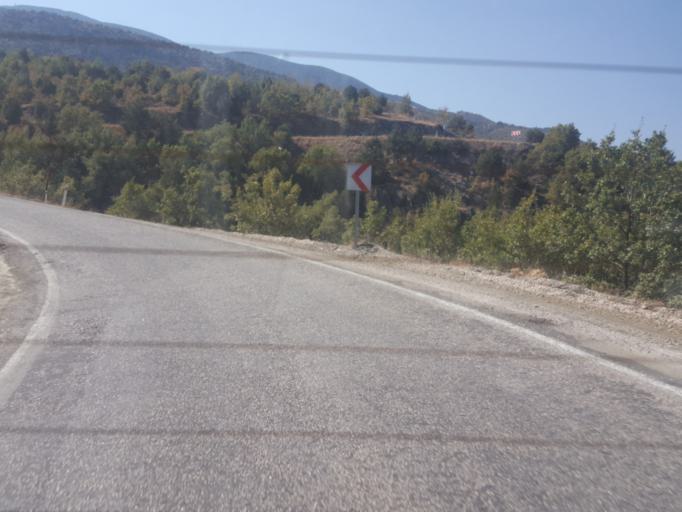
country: TR
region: Kastamonu
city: Tosya
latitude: 40.9944
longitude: 34.1675
